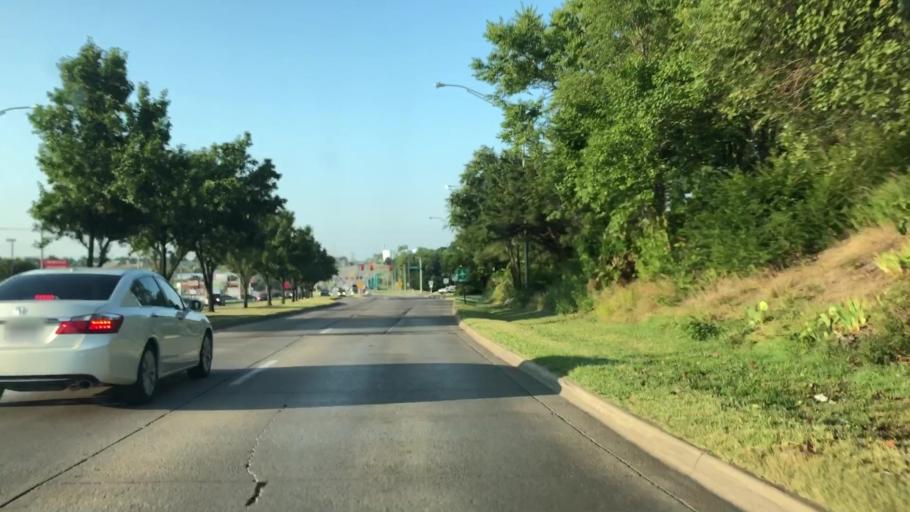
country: US
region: Oklahoma
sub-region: Washington County
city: Dewey
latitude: 36.7523
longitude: -95.9356
